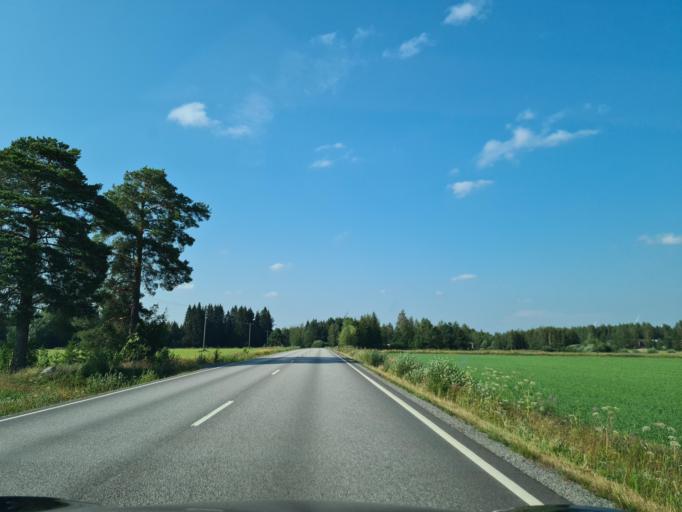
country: FI
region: Satakunta
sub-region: Pohjois-Satakunta
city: Karvia
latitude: 62.0540
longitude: 22.5143
